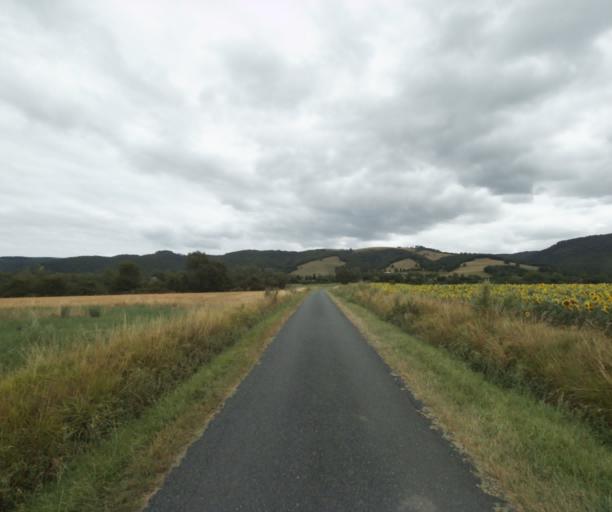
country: FR
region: Midi-Pyrenees
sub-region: Departement du Tarn
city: Soreze
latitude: 43.4619
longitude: 2.0727
